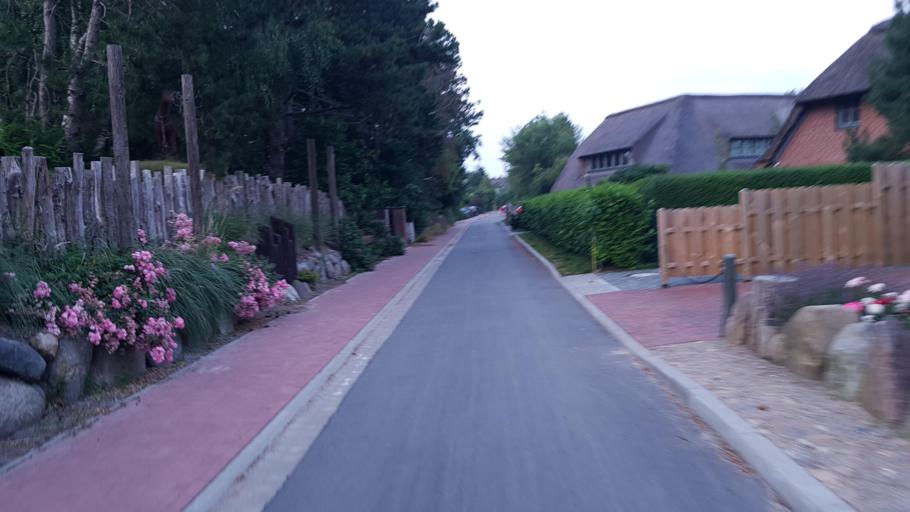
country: DE
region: Schleswig-Holstein
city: Sankt Peter-Ording
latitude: 54.2984
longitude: 8.6402
